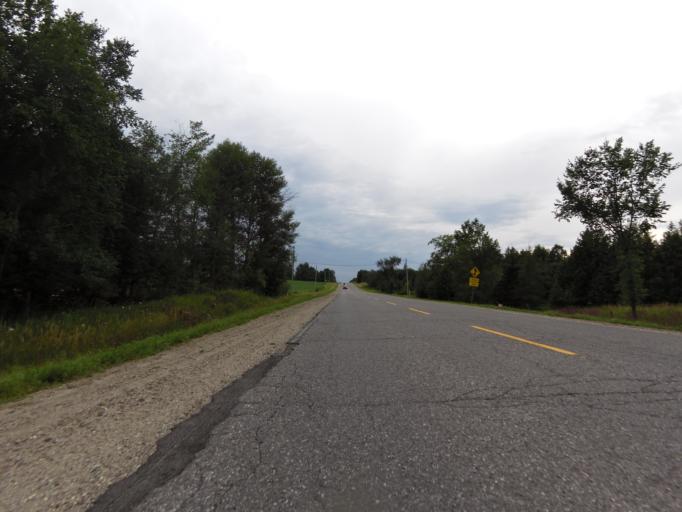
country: CA
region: Ontario
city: Carleton Place
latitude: 45.1274
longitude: -76.3364
